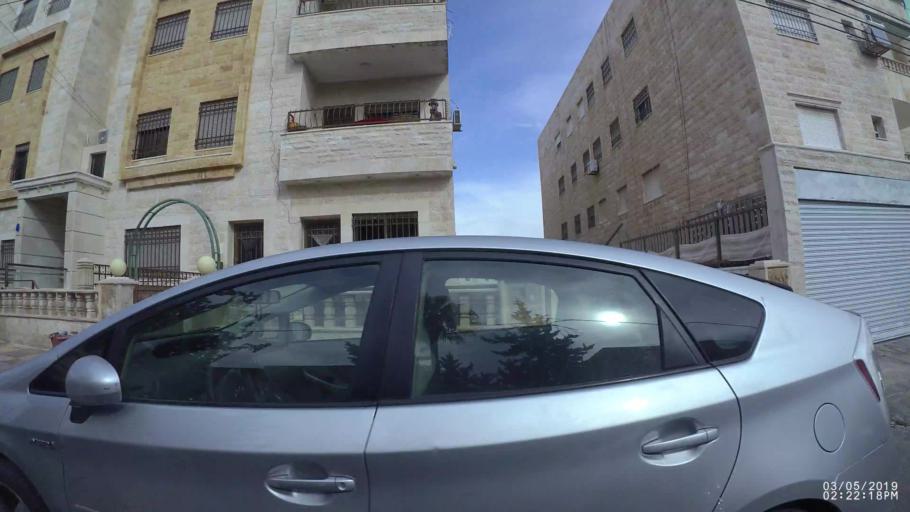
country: JO
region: Amman
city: Amman
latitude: 32.0099
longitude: 35.9363
